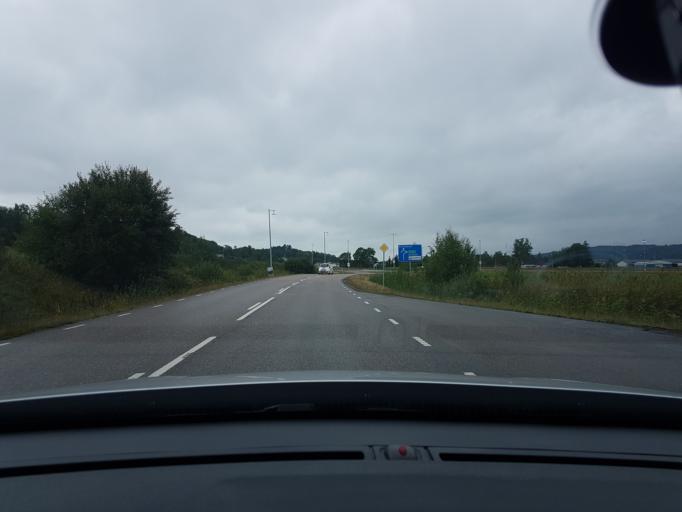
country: SE
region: Vaestra Goetaland
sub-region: Ale Kommun
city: Alvangen
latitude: 57.9675
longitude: 12.1540
